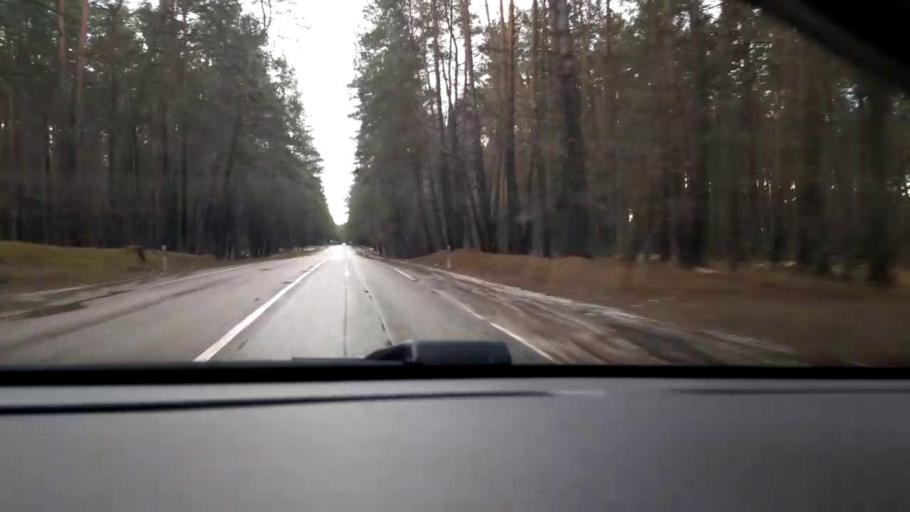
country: LT
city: Nemencine
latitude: 54.7804
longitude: 25.3838
